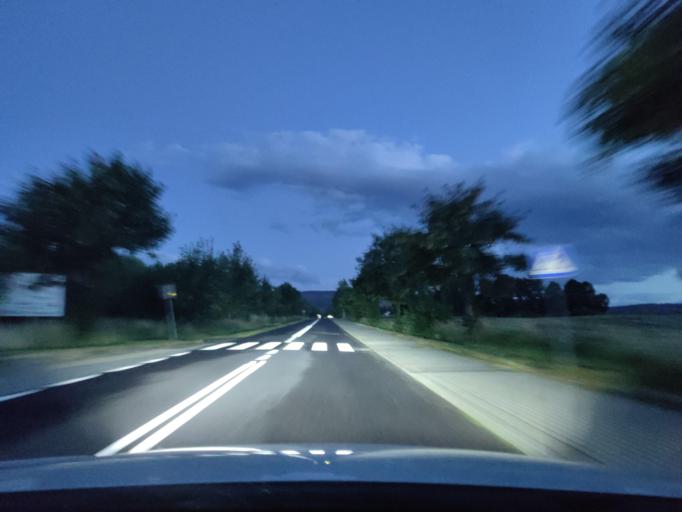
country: PL
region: Opole Voivodeship
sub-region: Powiat nyski
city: Glucholazy
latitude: 50.2896
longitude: 17.3896
